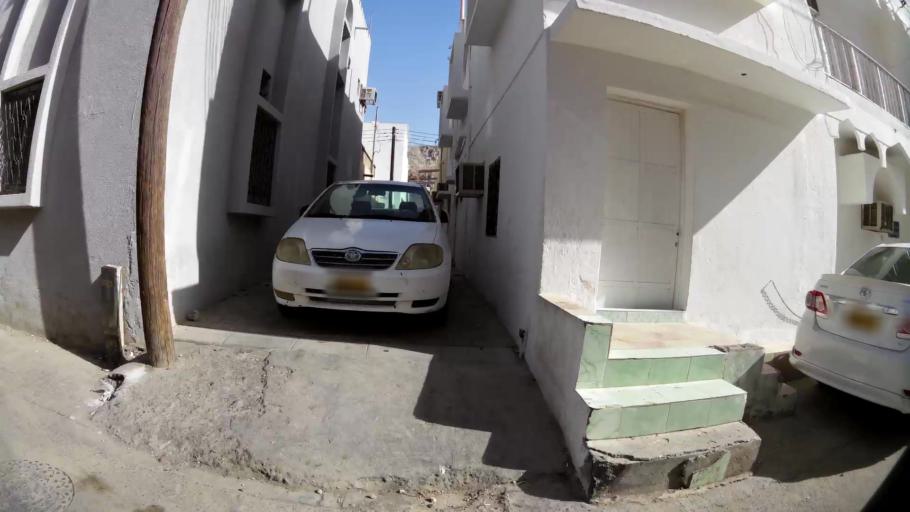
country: OM
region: Muhafazat Masqat
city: Muscat
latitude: 23.5856
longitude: 58.5169
